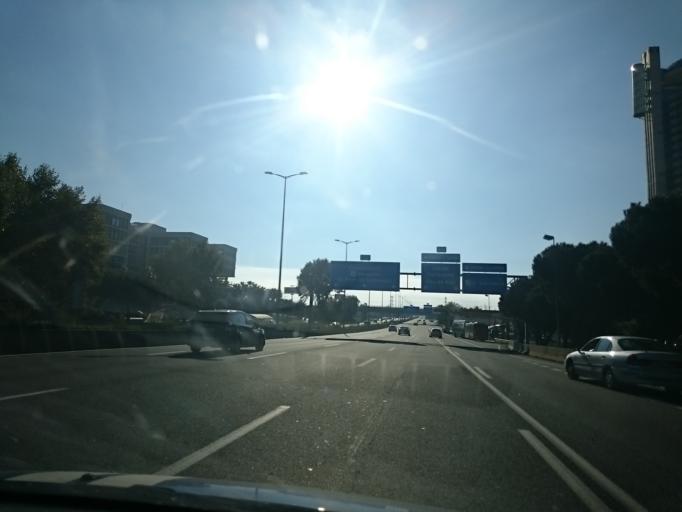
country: ES
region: Catalonia
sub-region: Provincia de Barcelona
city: L'Hospitalet de Llobregat
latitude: 41.3467
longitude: 2.1110
